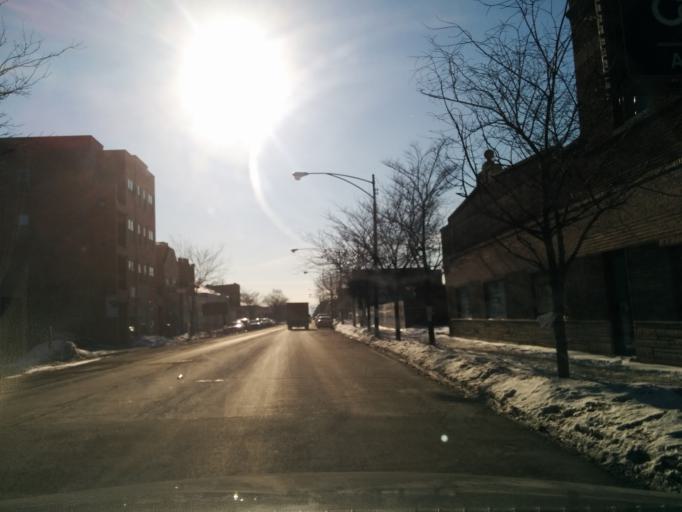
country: US
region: Illinois
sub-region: Cook County
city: Lincolnwood
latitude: 41.9456
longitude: -87.7347
